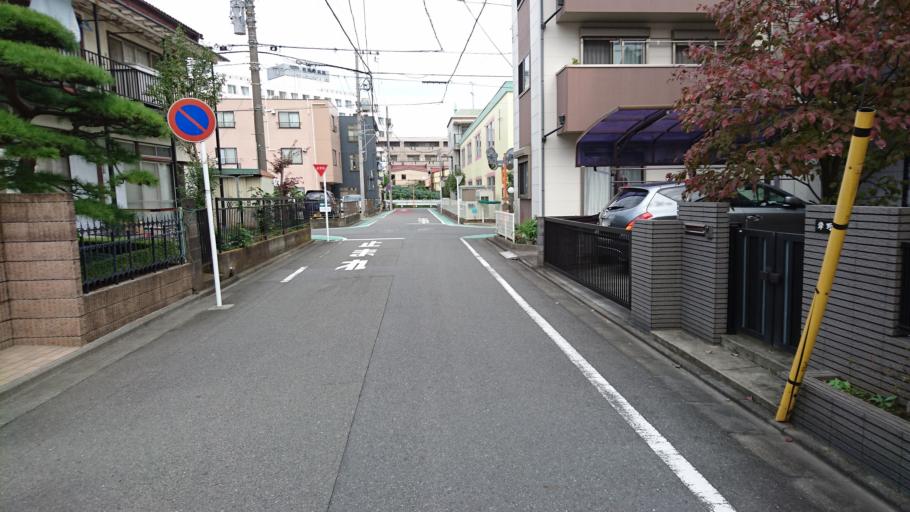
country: JP
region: Tokyo
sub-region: Machida-shi
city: Machida
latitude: 35.5714
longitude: 139.3881
